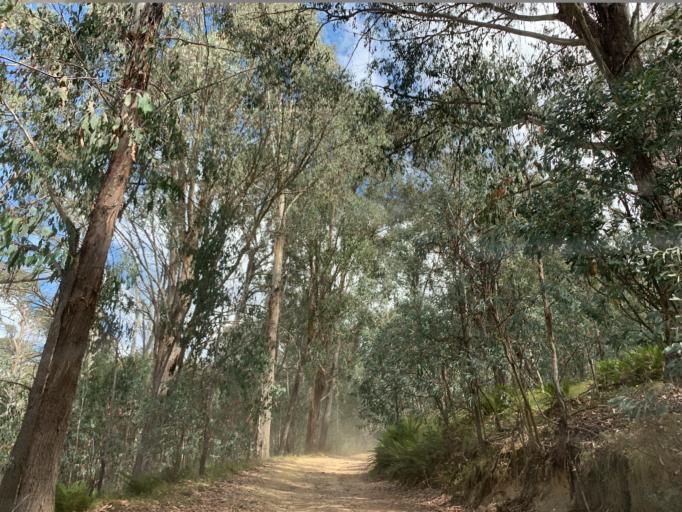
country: AU
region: Victoria
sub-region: Mansfield
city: Mansfield
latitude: -37.1082
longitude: 146.5349
